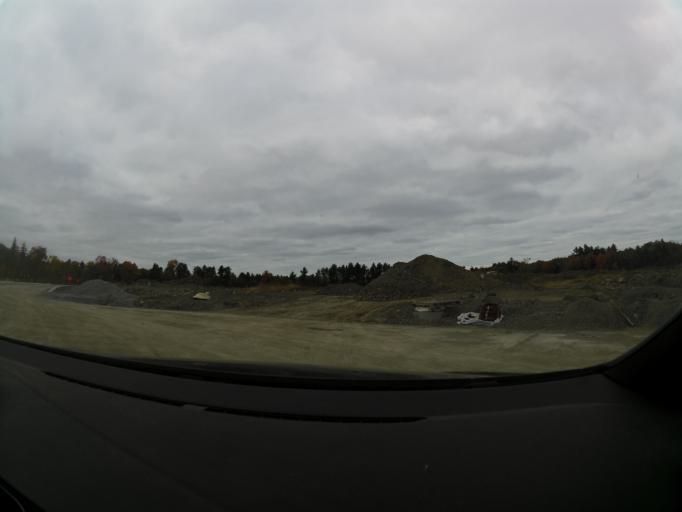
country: CA
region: Ontario
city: Bells Corners
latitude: 45.3364
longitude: -75.9400
